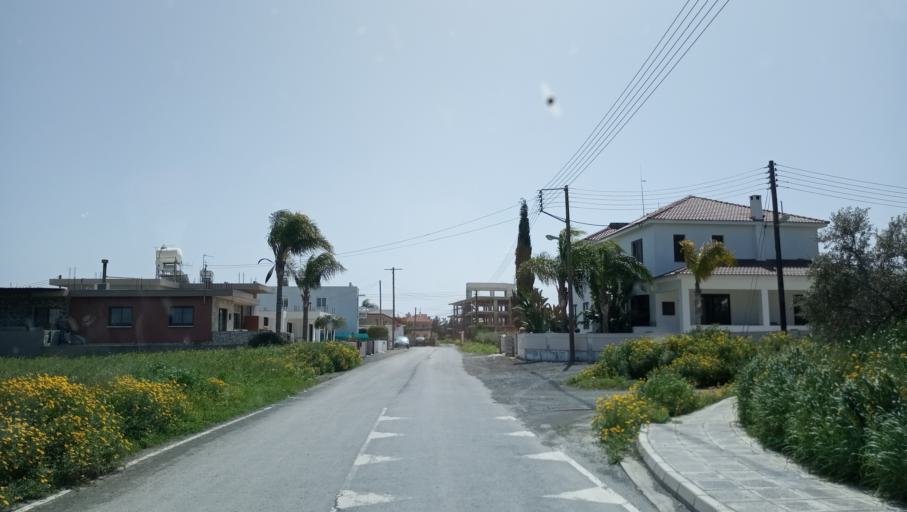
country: CY
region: Lefkosia
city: Alampra
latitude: 35.0080
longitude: 33.3927
